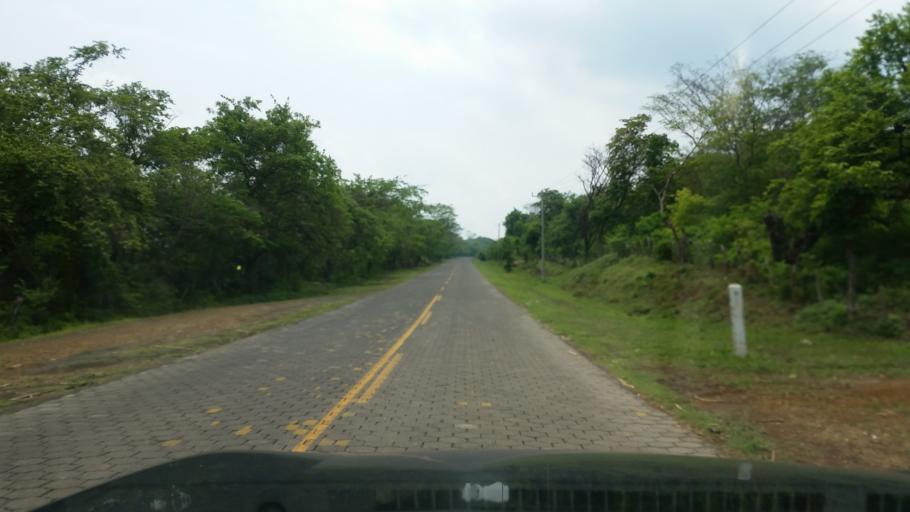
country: NI
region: Managua
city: San Rafael del Sur
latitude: 11.8721
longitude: -86.5148
